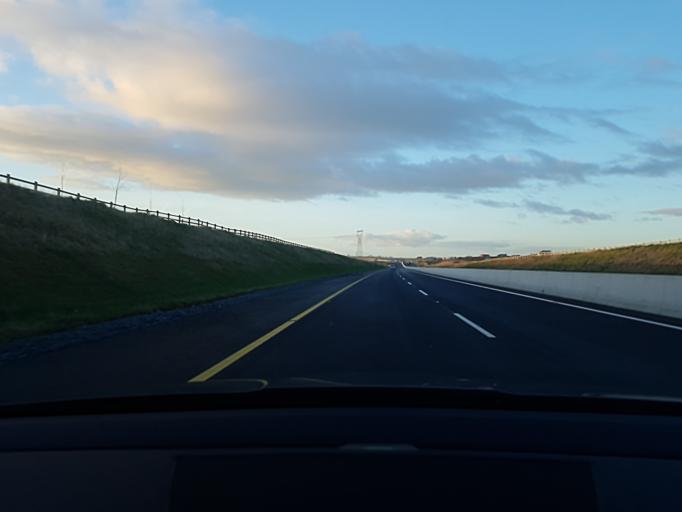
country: IE
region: Connaught
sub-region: County Galway
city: Athenry
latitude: 53.3770
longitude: -8.7956
